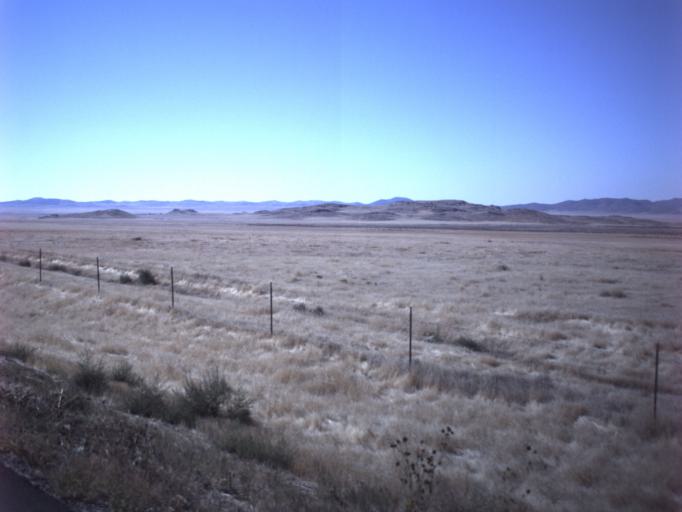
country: US
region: Utah
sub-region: Tooele County
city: Grantsville
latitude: 40.4151
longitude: -112.7487
